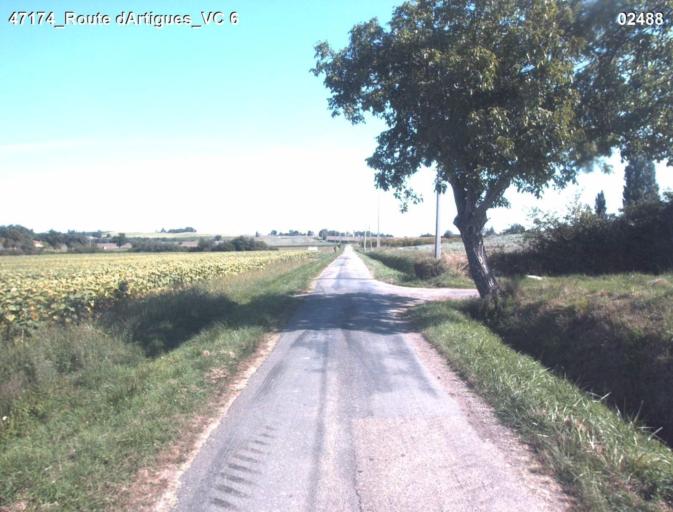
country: FR
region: Midi-Pyrenees
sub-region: Departement du Gers
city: Condom
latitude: 44.0289
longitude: 0.3342
